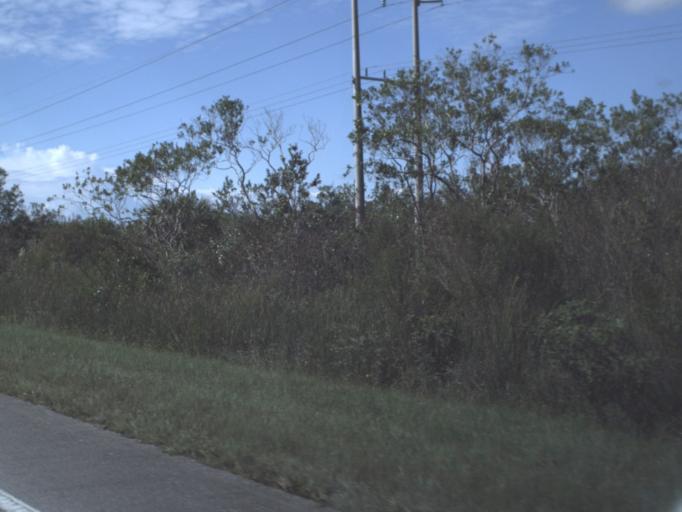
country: US
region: Florida
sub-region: Collier County
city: Lely Resort
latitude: 26.0127
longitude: -81.3461
